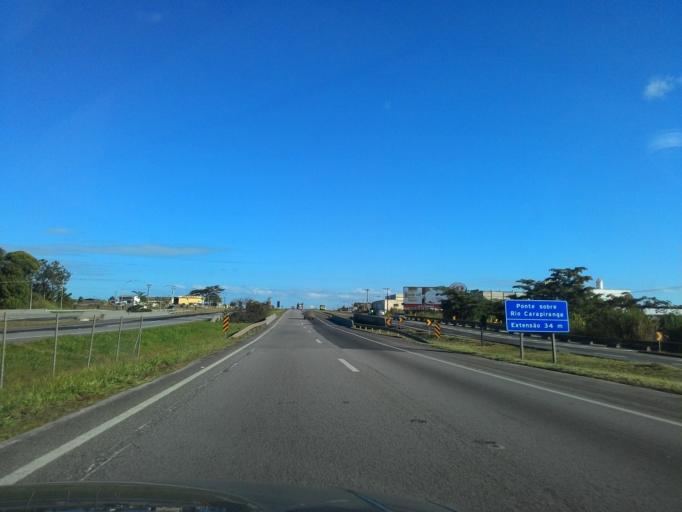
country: BR
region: Sao Paulo
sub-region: Registro
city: Registro
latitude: -24.5099
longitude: -47.8498
